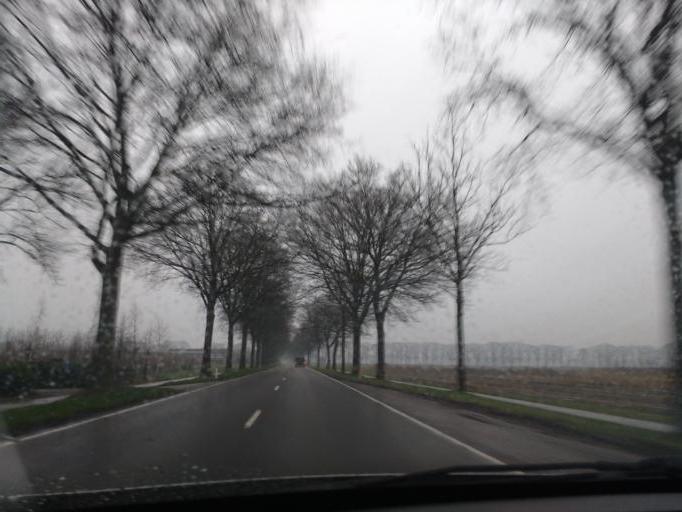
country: NL
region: North Brabant
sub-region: Gemeente Asten
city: Asten
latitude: 51.4829
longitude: 5.8385
